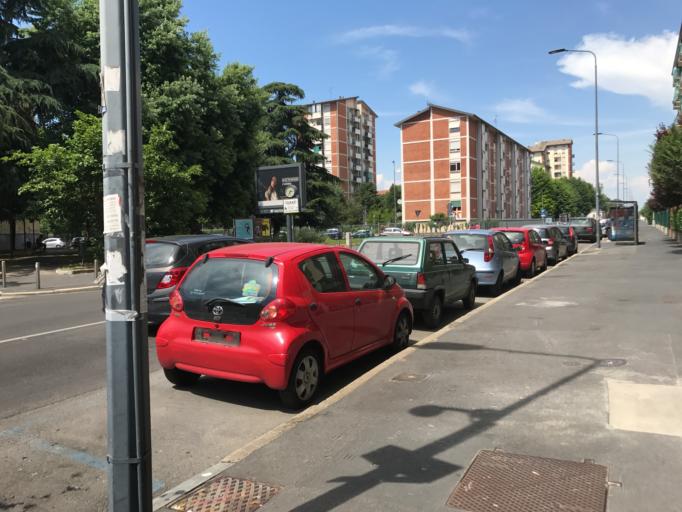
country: IT
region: Lombardy
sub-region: Citta metropolitana di Milano
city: Bresso
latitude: 45.5093
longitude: 9.1995
